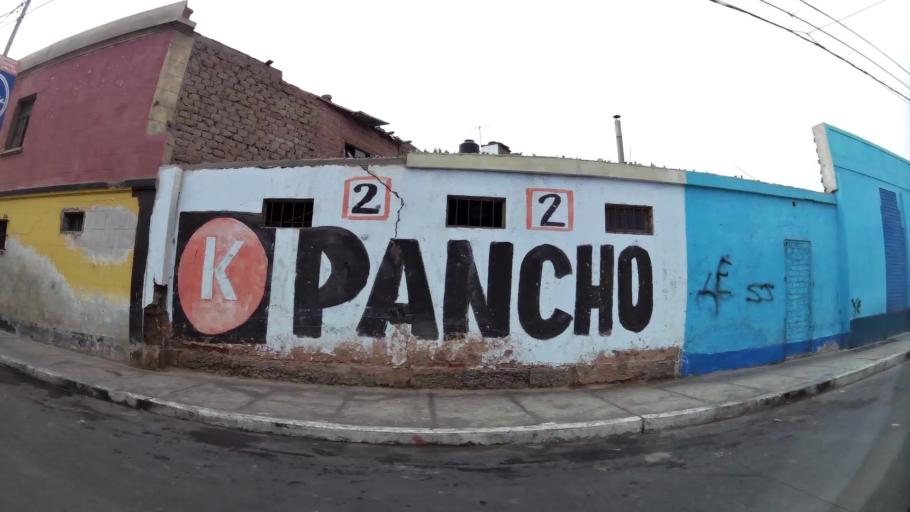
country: PE
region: Callao
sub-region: Callao
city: Callao
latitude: -12.0589
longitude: -77.1360
